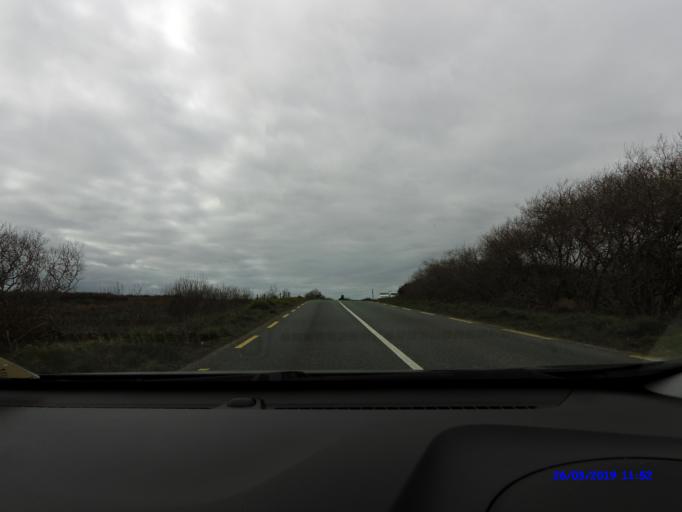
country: IE
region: Connaught
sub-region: Maigh Eo
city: Belmullet
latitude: 54.1753
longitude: -9.8434
